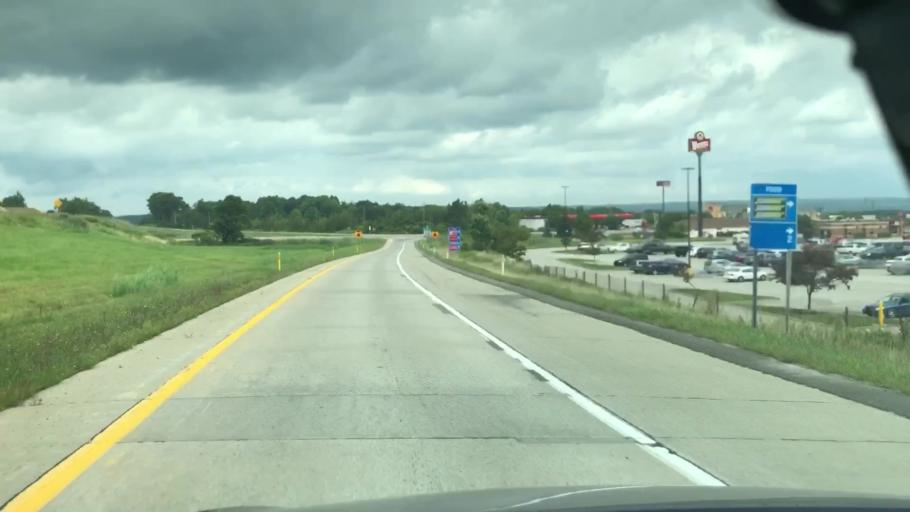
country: US
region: Pennsylvania
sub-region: Erie County
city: Edinboro
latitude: 41.8773
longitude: -80.1759
